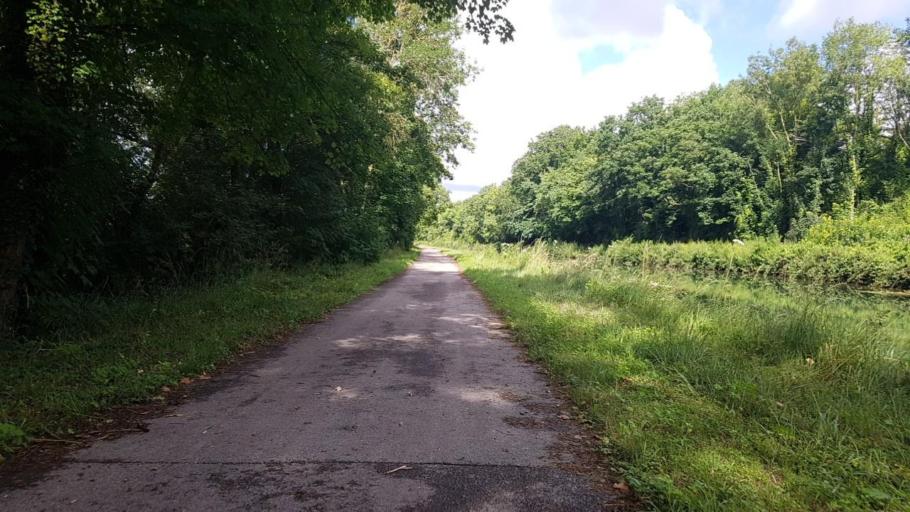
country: FR
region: Champagne-Ardenne
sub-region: Departement de la Marne
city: Tours-sur-Marne
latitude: 49.0419
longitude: 4.1632
